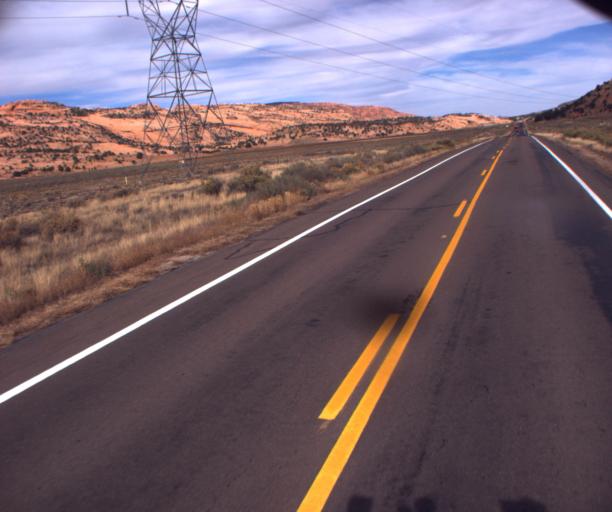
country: US
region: Arizona
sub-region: Navajo County
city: Kayenta
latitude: 36.6226
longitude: -110.4616
